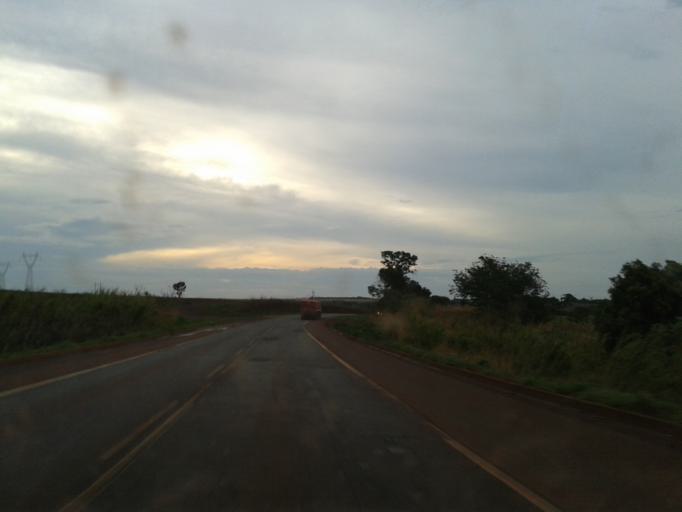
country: BR
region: Goias
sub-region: Santa Helena De Goias
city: Santa Helena de Goias
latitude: -17.9554
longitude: -50.5062
